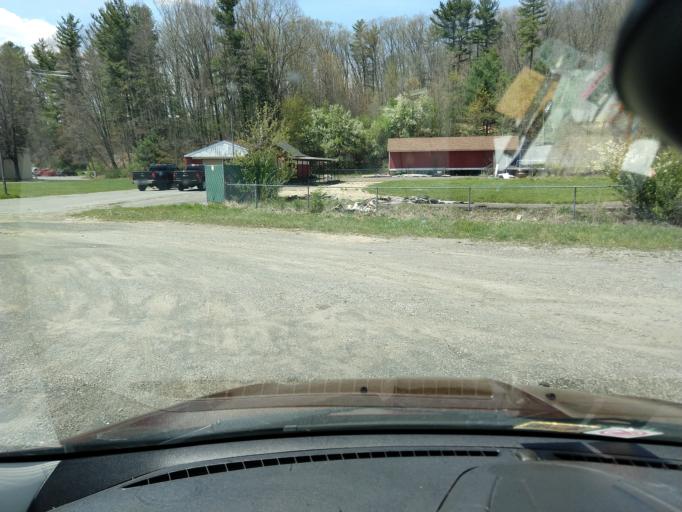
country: US
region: West Virginia
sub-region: Raleigh County
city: Stanaford
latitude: 37.8117
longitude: -81.1746
